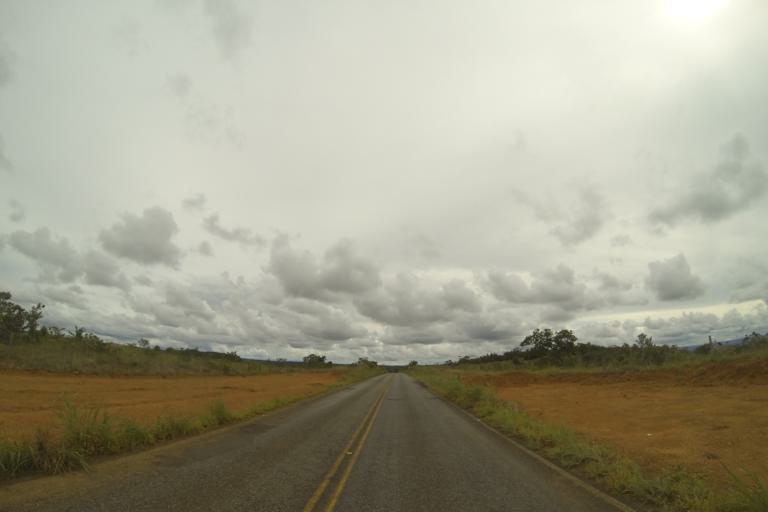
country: BR
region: Minas Gerais
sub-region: Ibia
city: Ibia
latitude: -19.6798
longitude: -46.4422
